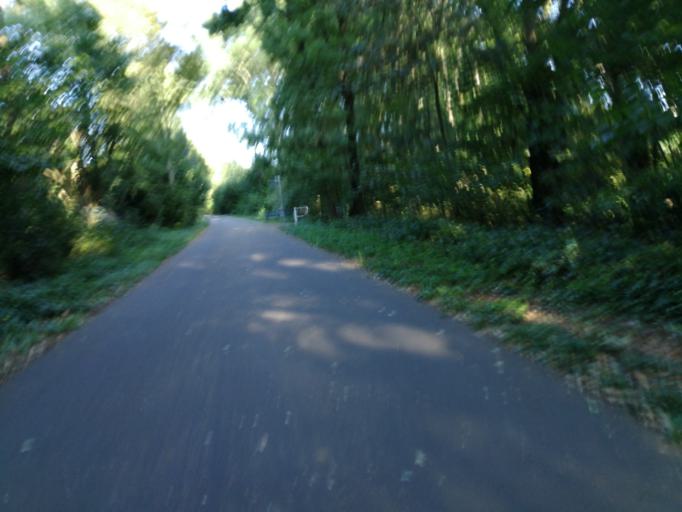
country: DE
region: North Rhine-Westphalia
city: Opladen
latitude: 51.0718
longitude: 7.0266
